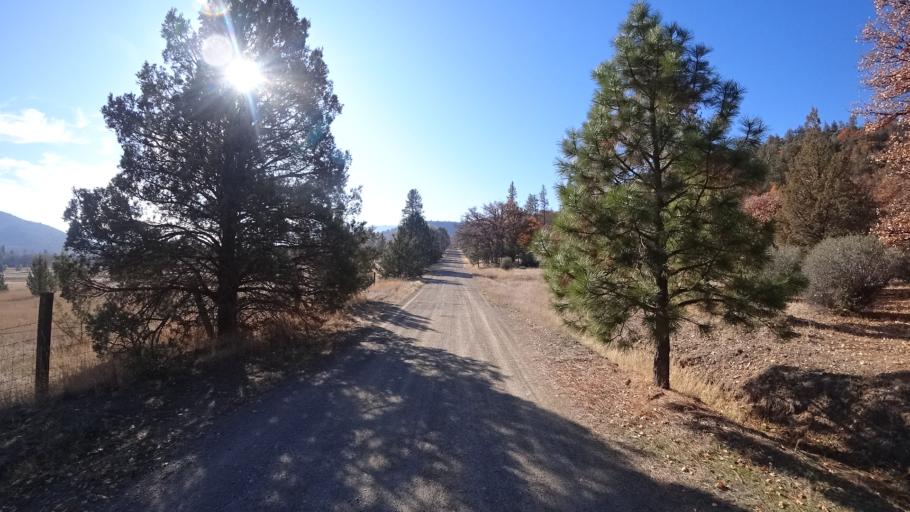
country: US
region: California
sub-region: Siskiyou County
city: Yreka
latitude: 41.6982
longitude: -122.6510
